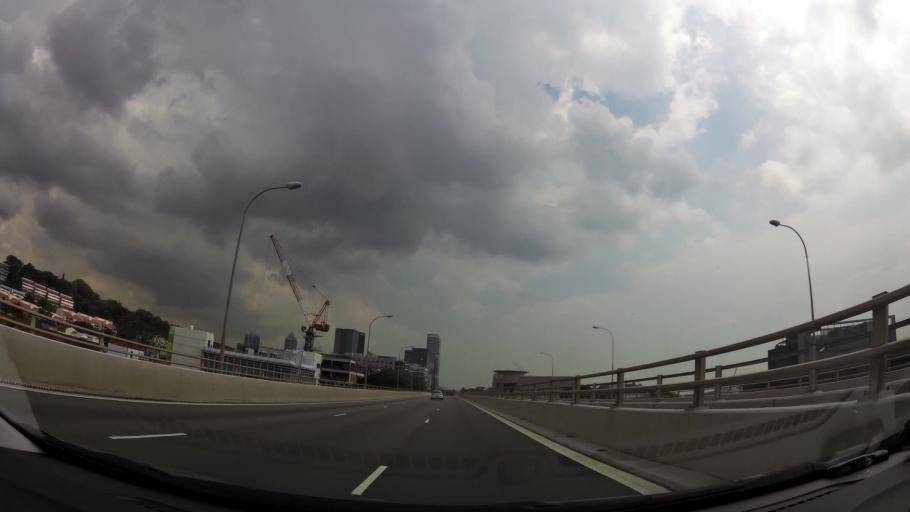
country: SG
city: Singapore
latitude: 1.2770
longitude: 103.7902
